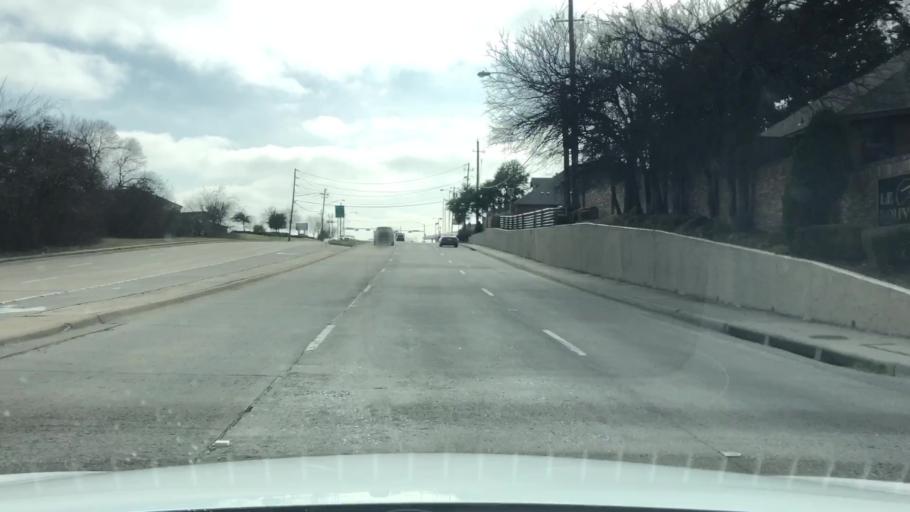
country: US
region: Texas
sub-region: Dallas County
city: Addison
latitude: 33.0055
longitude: -96.8574
